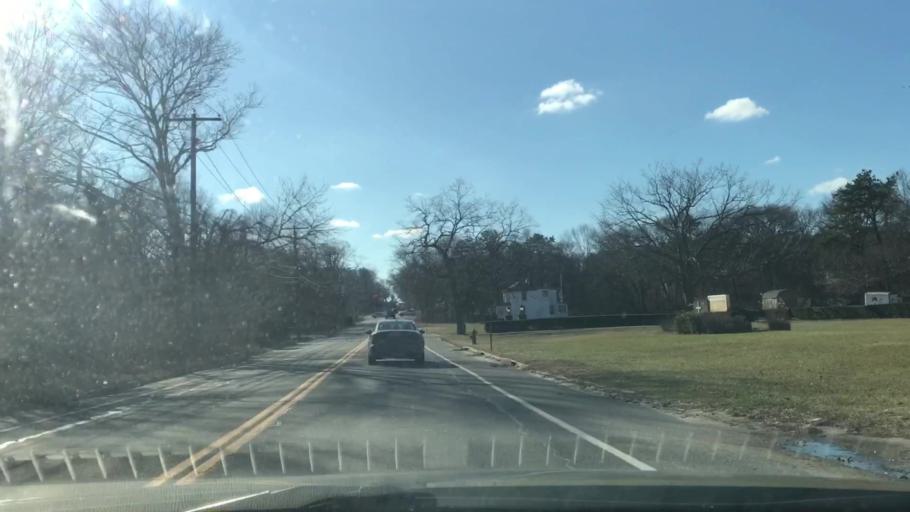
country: US
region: New York
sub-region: Suffolk County
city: Riverhead
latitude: 40.9418
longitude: -72.6569
